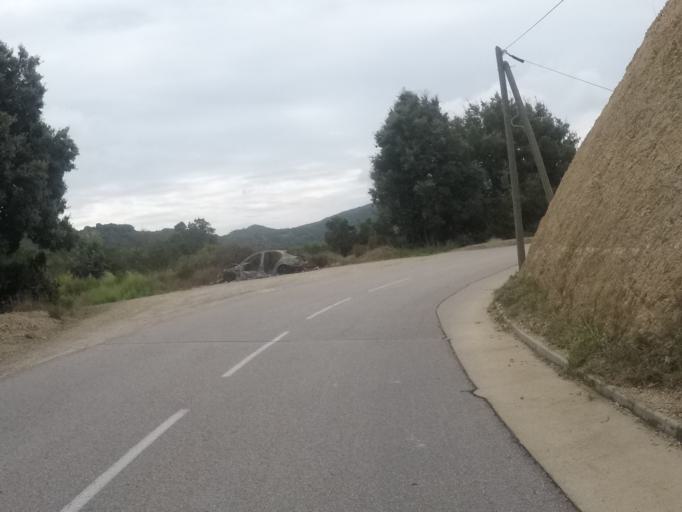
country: FR
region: Corsica
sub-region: Departement de la Corse-du-Sud
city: Pietrosella
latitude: 41.8079
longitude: 8.8438
